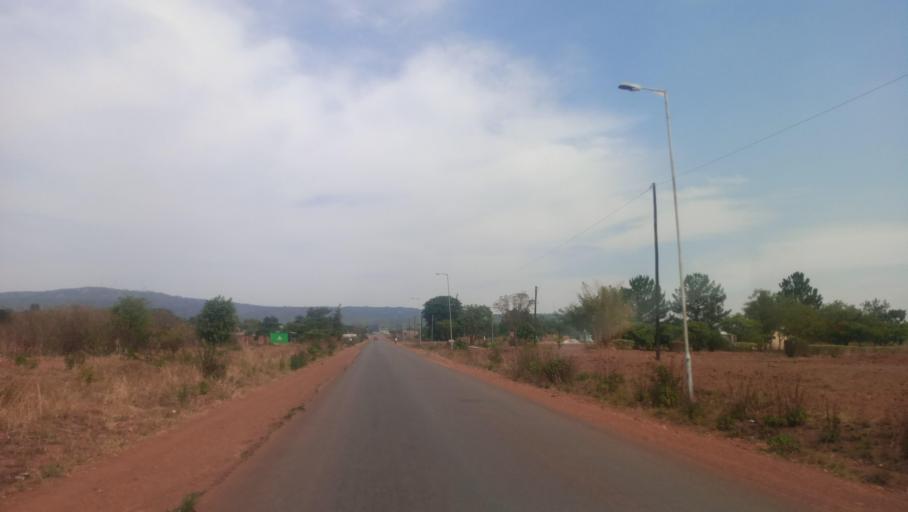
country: ZM
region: Northern
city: Mpika
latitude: -11.8389
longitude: 31.4342
